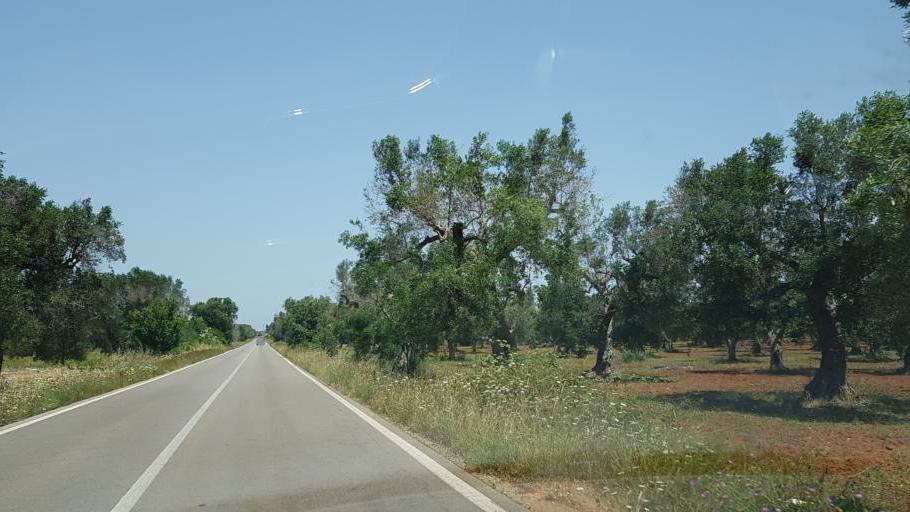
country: IT
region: Apulia
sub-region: Provincia di Lecce
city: Veglie
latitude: 40.3202
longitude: 17.9236
